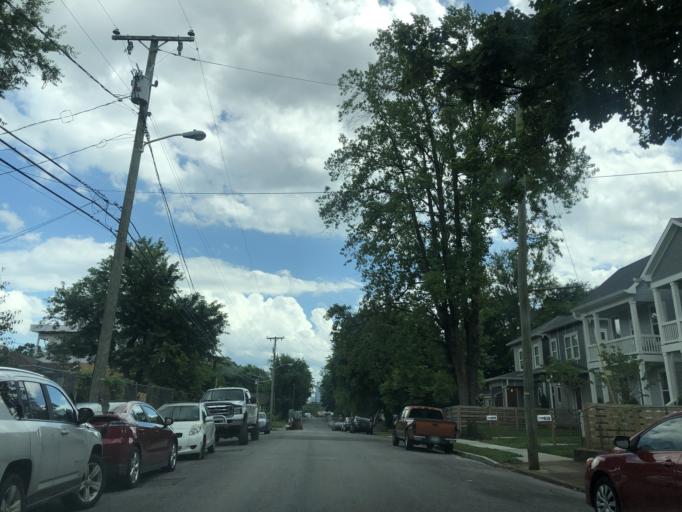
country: US
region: Tennessee
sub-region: Davidson County
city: Nashville
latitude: 36.1827
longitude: -86.7715
